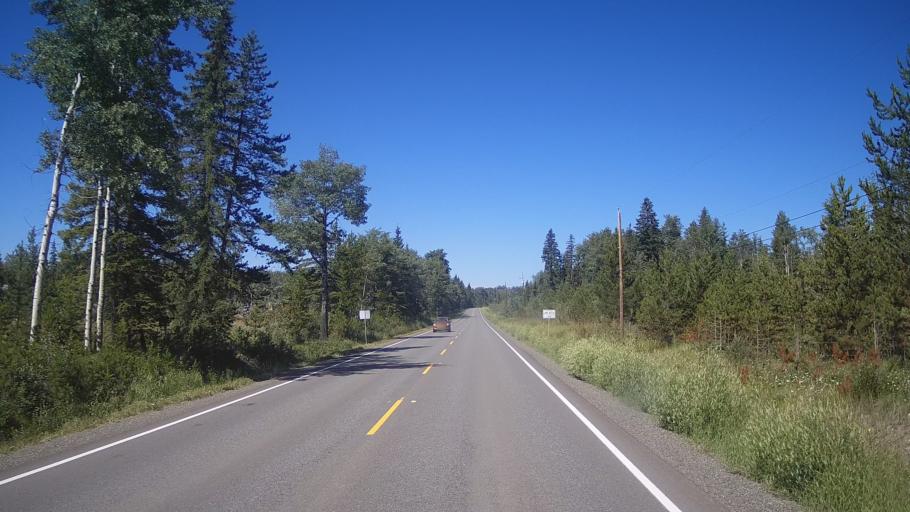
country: CA
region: British Columbia
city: Cache Creek
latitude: 51.5402
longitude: -121.0401
